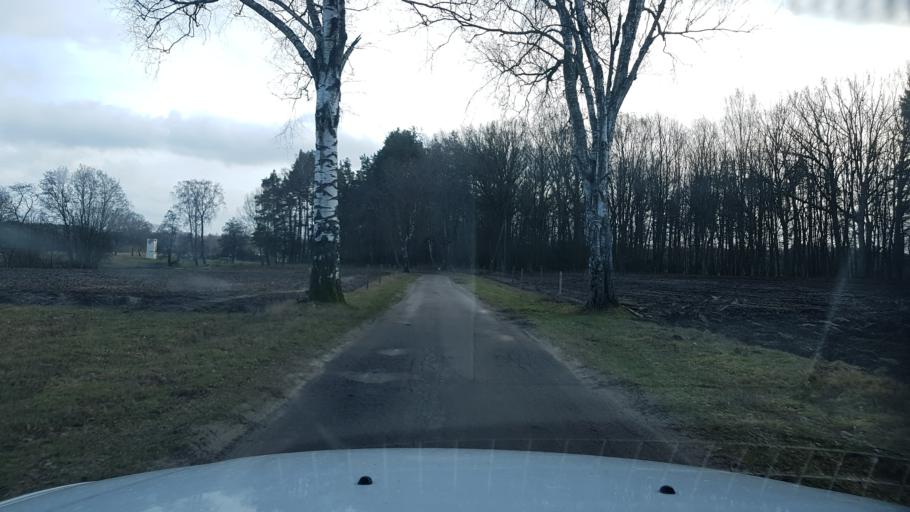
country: PL
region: West Pomeranian Voivodeship
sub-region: Powiat szczecinecki
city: Borne Sulinowo
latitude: 53.6253
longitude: 16.6134
